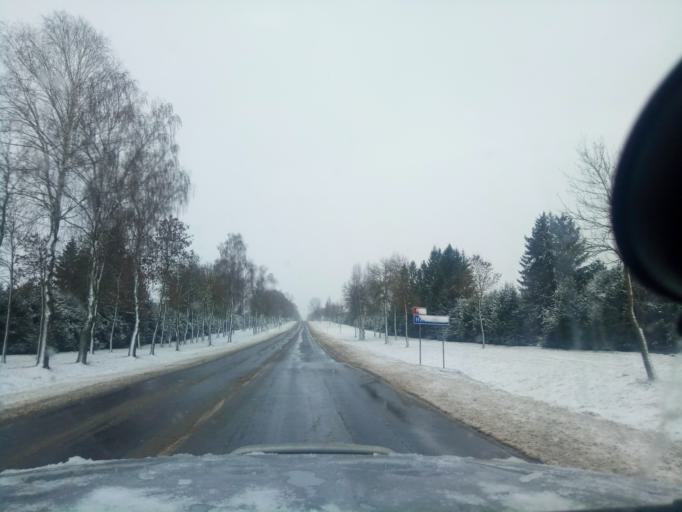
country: BY
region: Minsk
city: Haradzyeya
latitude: 53.3591
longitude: 26.5145
